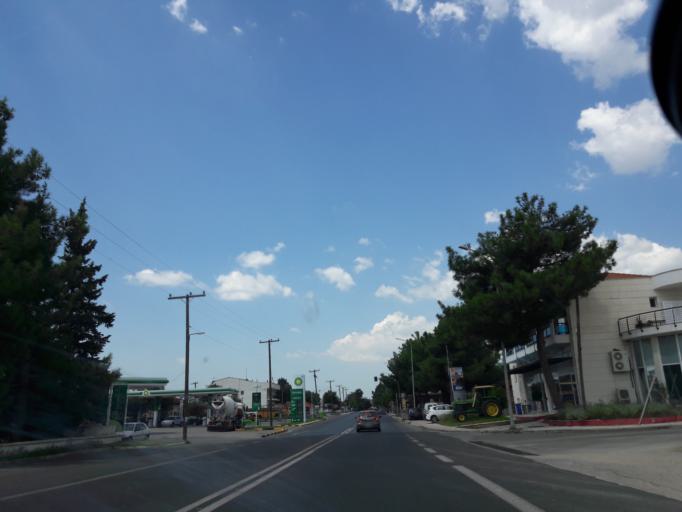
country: GR
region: Central Macedonia
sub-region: Nomos Thessalonikis
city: Agia Paraskevi
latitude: 40.5217
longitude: 23.0560
